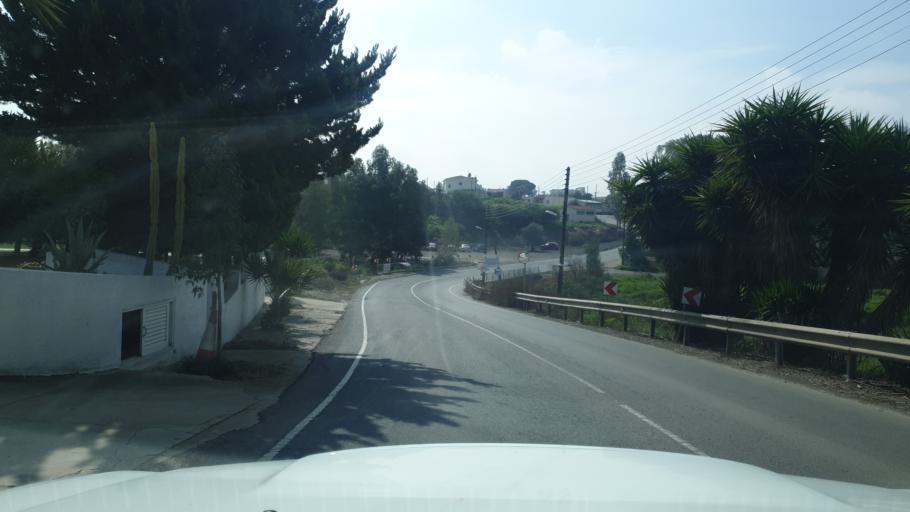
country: CY
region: Lefkosia
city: Kato Deftera
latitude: 35.0892
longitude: 33.2777
